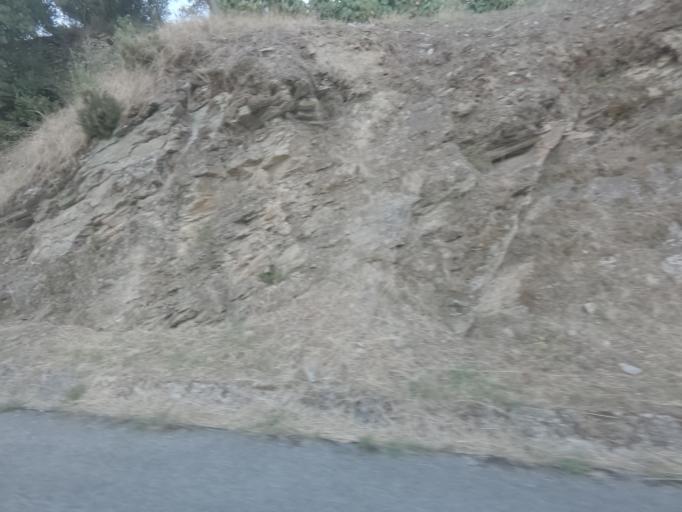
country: PT
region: Viseu
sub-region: Armamar
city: Armamar
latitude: 41.1613
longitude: -7.6841
